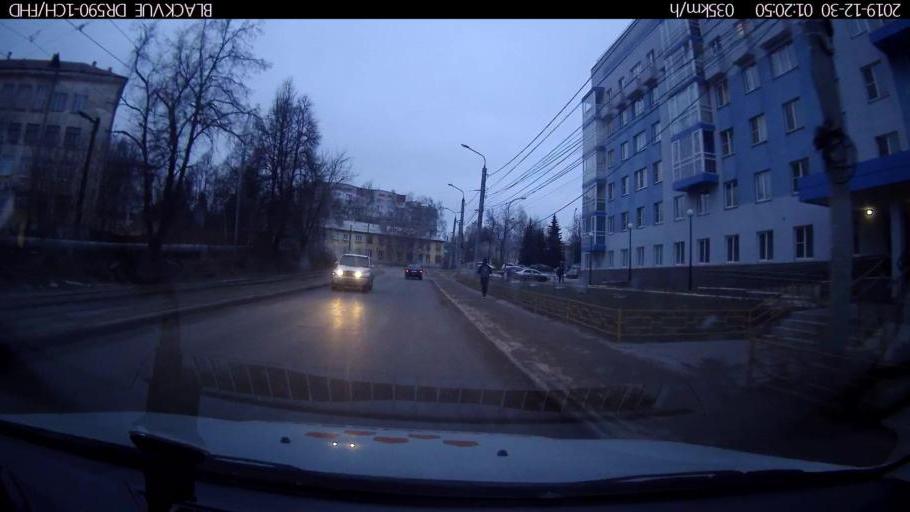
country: RU
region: Nizjnij Novgorod
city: Nizhniy Novgorod
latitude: 56.3027
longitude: 43.9902
